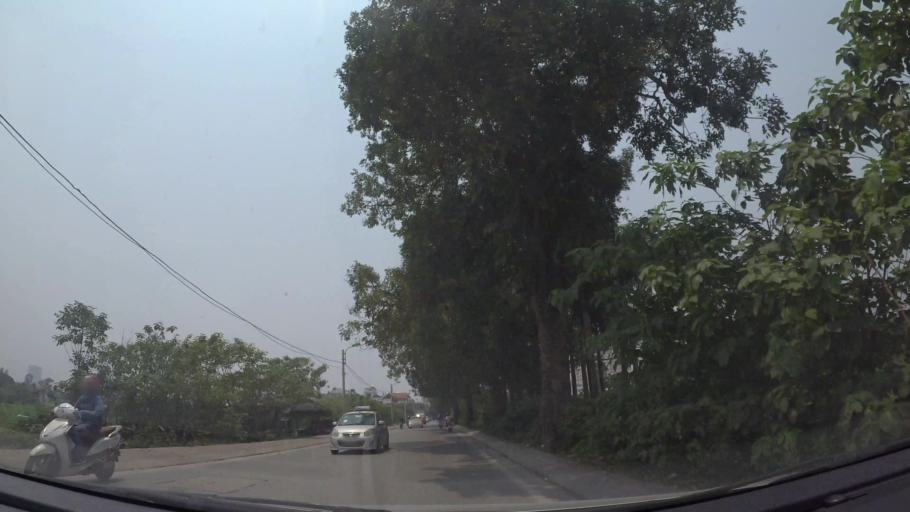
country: VN
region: Ha Noi
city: Thanh Xuan
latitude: 20.9915
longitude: 105.7814
